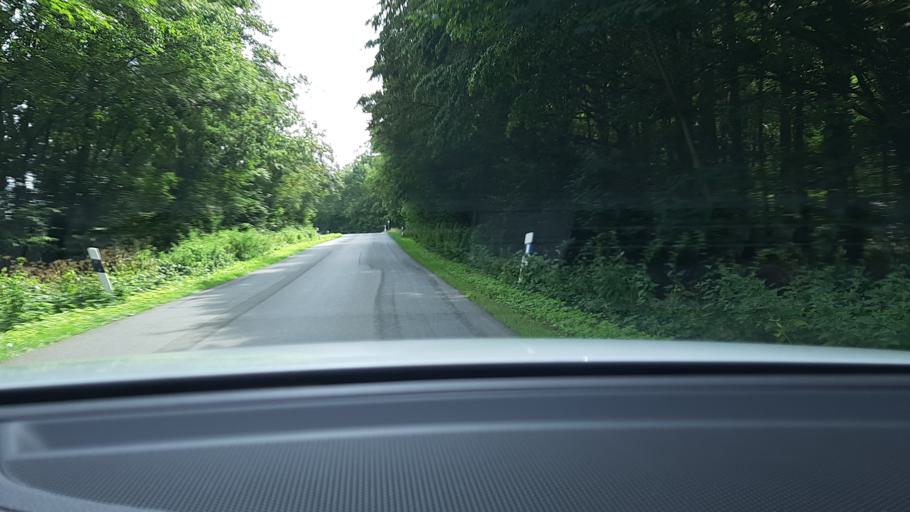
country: DE
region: Schleswig-Holstein
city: Reinfeld
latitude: 53.8460
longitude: 10.4707
